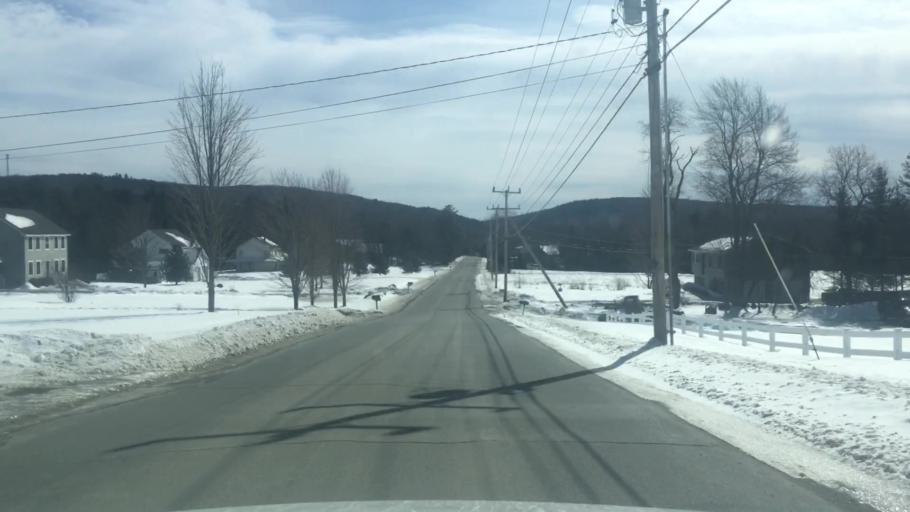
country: US
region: Maine
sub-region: Penobscot County
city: Holden
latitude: 44.7454
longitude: -68.6312
